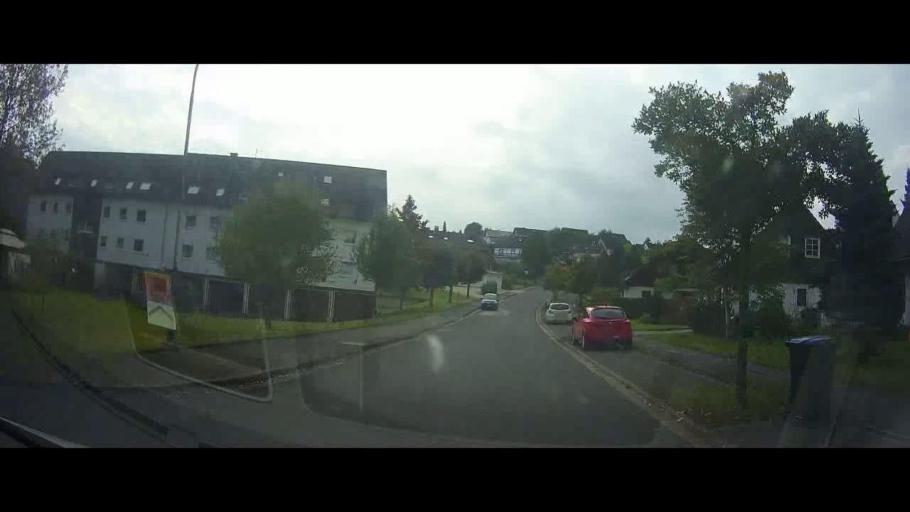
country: DE
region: Lower Saxony
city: Uslar
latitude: 51.6271
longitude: 9.6609
